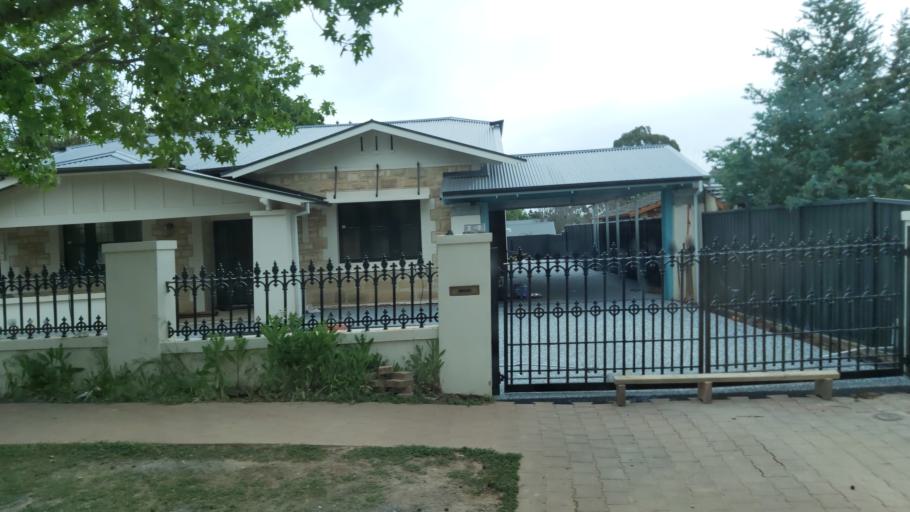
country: AU
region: South Australia
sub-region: Burnside
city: Glenunga
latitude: -34.9579
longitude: 138.6361
